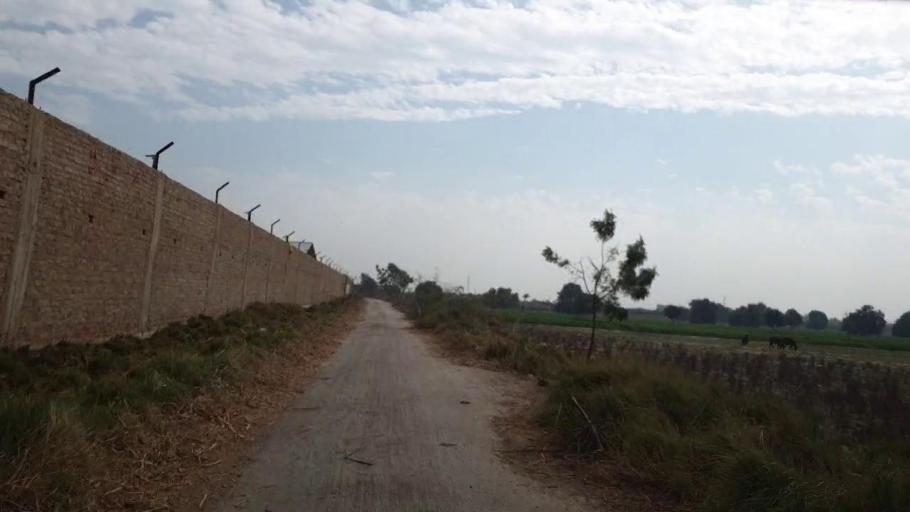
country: PK
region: Sindh
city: Matiari
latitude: 25.5799
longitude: 68.4412
